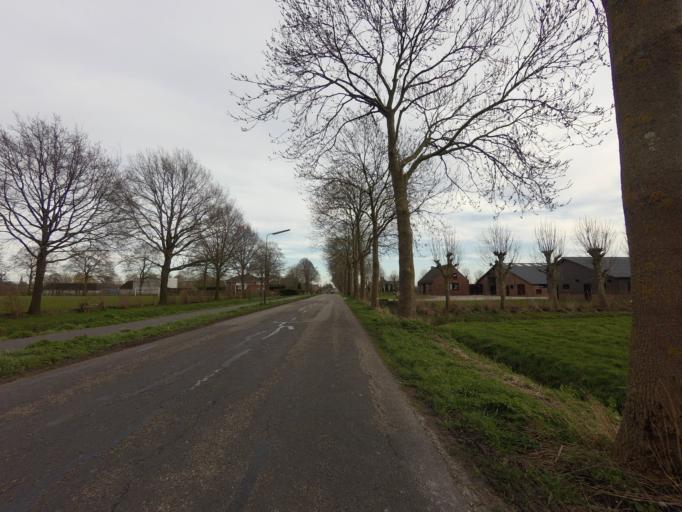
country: NL
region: Utrecht
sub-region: Gemeente De Ronde Venen
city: Mijdrecht
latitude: 52.1988
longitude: 4.8542
